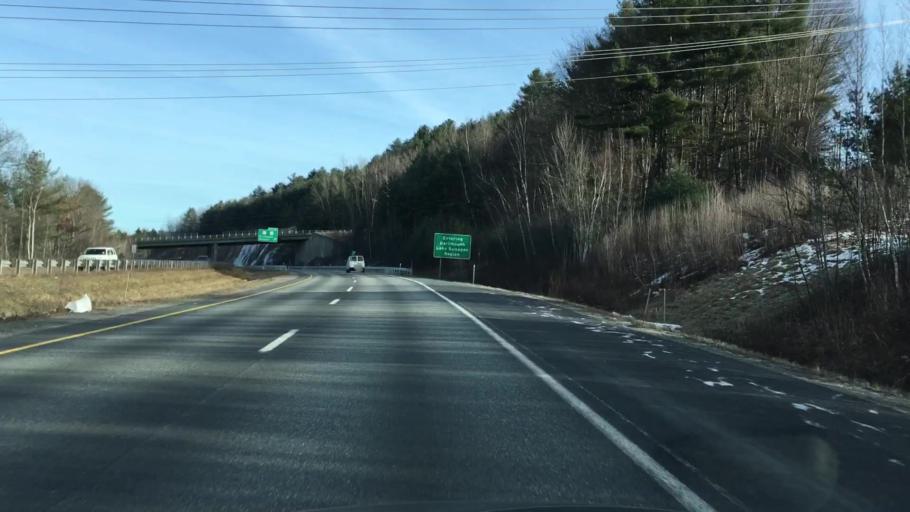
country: US
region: Vermont
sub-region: Windsor County
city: White River Junction
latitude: 43.6350
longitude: -72.2882
